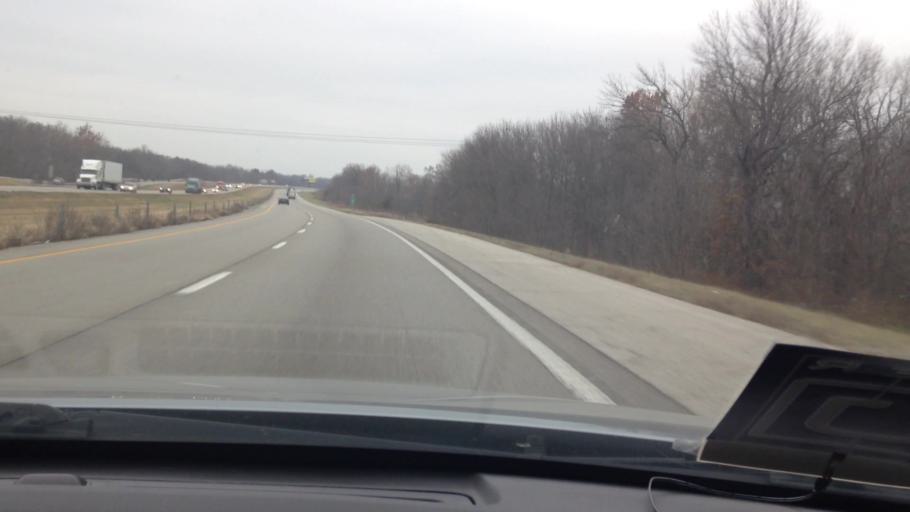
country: US
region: Missouri
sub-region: Cass County
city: Peculiar
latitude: 38.7577
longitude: -94.4832
